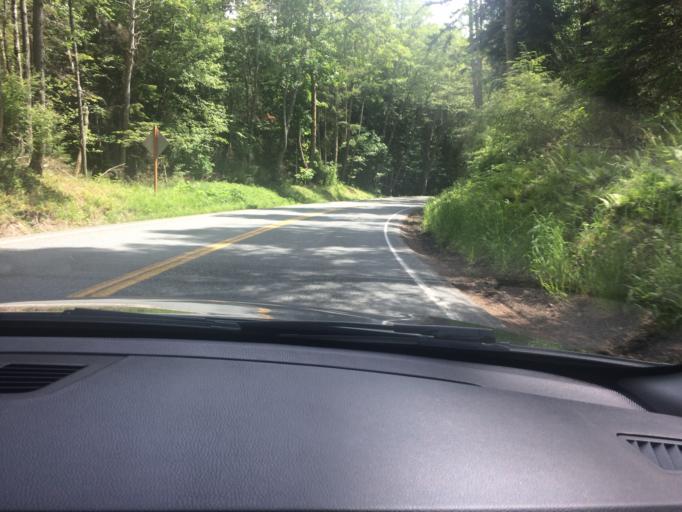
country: US
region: Washington
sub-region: Island County
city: Ault Field
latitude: 48.4206
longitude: -122.6517
